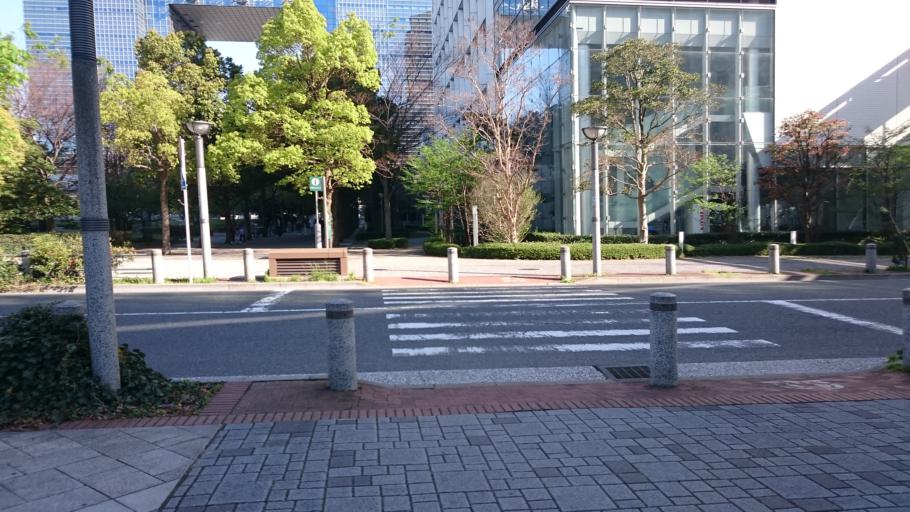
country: JP
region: Tokyo
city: Tokyo
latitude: 35.6189
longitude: 139.7780
